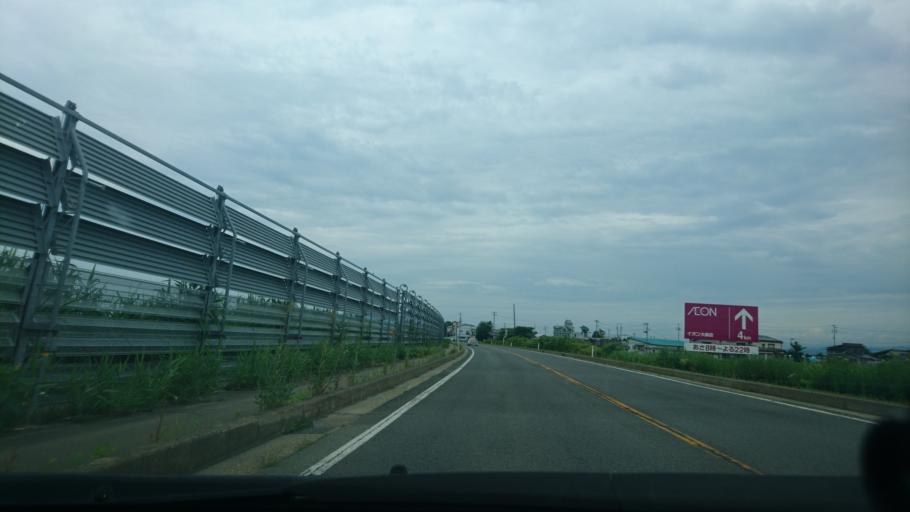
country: JP
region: Akita
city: Omagari
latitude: 39.4197
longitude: 140.5391
